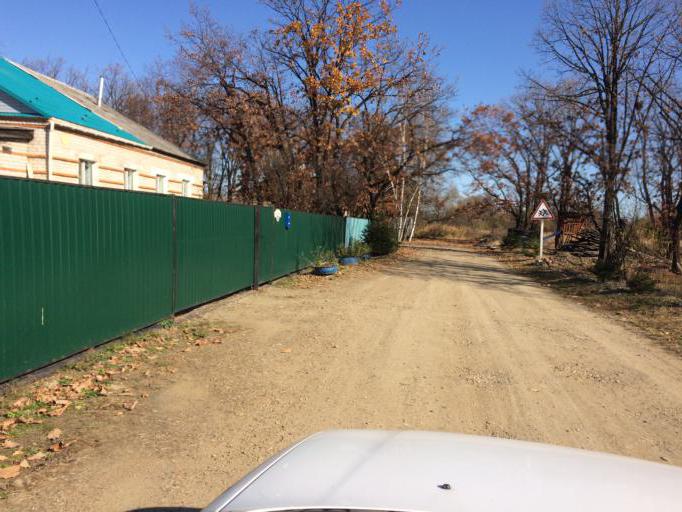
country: RU
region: Primorskiy
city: Dal'nerechensk
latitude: 45.9129
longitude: 133.8070
